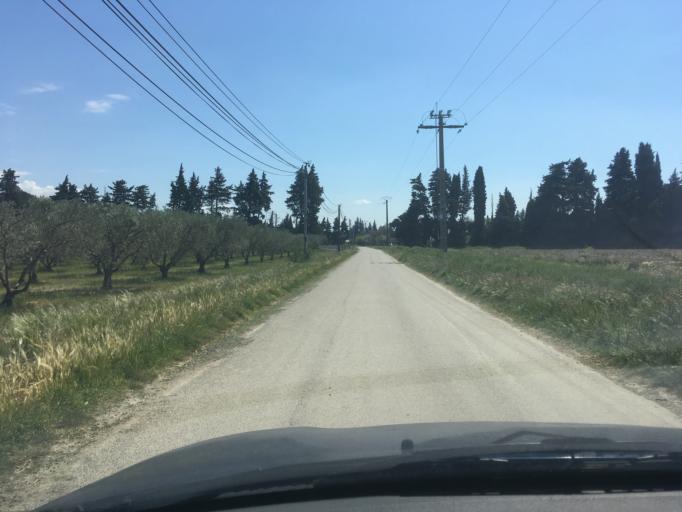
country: FR
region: Provence-Alpes-Cote d'Azur
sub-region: Departement du Vaucluse
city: Jonquieres
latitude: 44.1079
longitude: 4.9361
